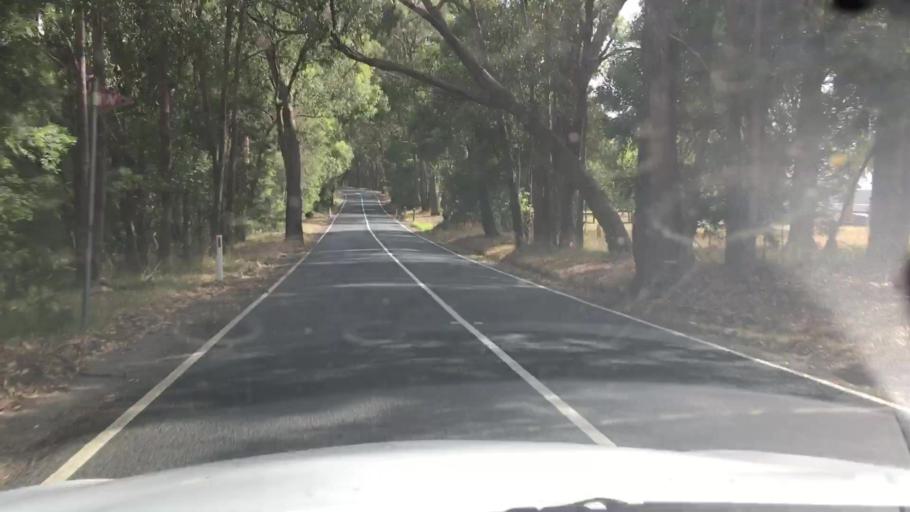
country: AU
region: Victoria
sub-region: Yarra Ranges
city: Macclesfield
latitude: -37.8426
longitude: 145.4861
